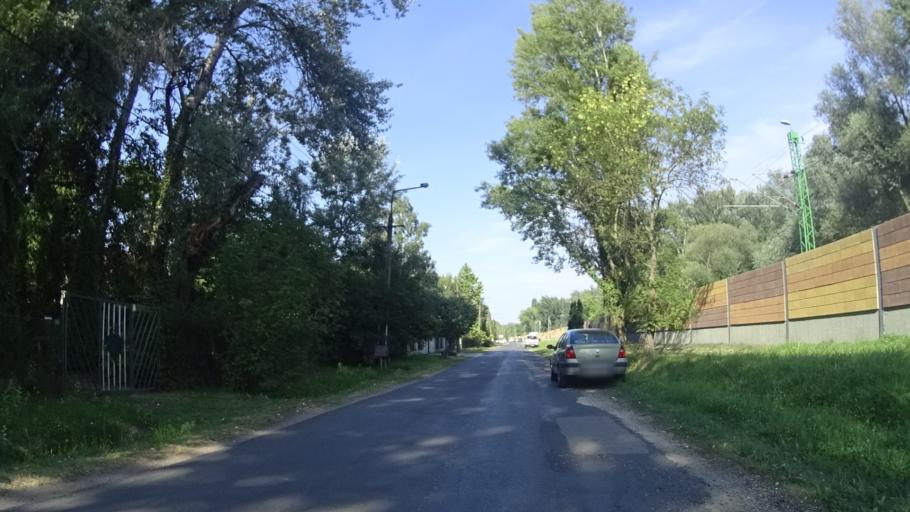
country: HU
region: Somogy
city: Balatonszarszo
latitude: 46.8368
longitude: 17.8426
